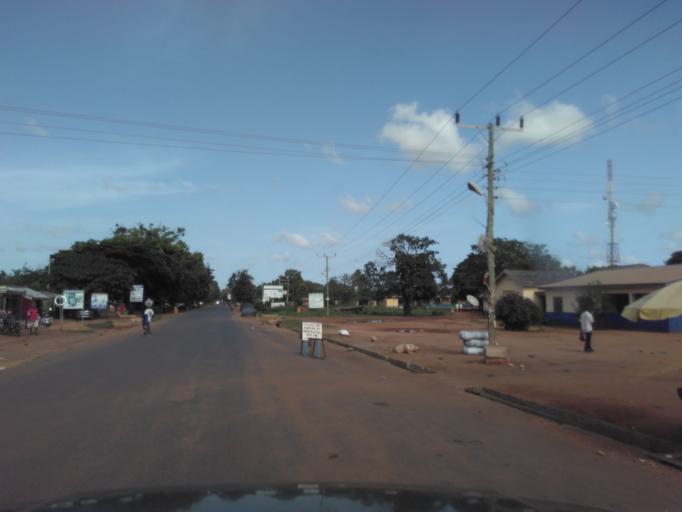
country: GH
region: Volta
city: Anloga
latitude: 5.8970
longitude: 0.5227
